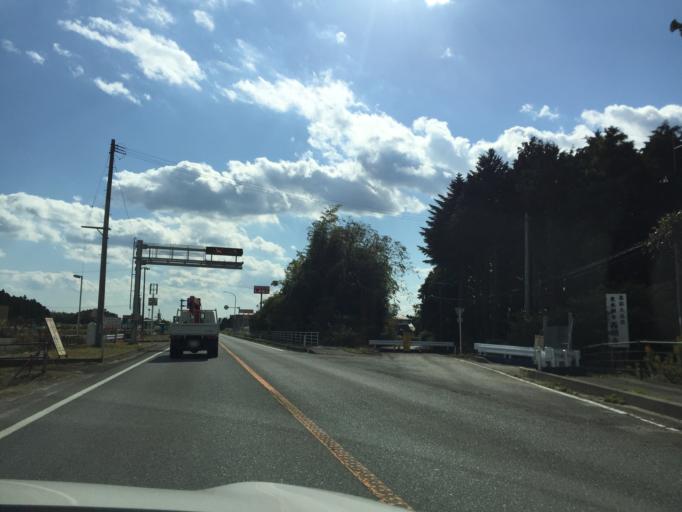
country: JP
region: Fukushima
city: Namie
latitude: 37.3636
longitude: 141.0095
